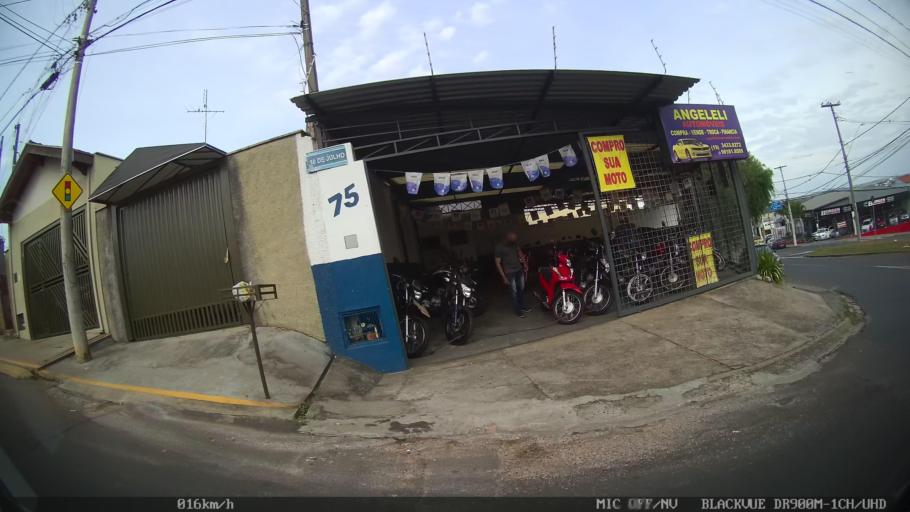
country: BR
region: Sao Paulo
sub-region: Piracicaba
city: Piracicaba
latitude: -22.7448
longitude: -47.6234
